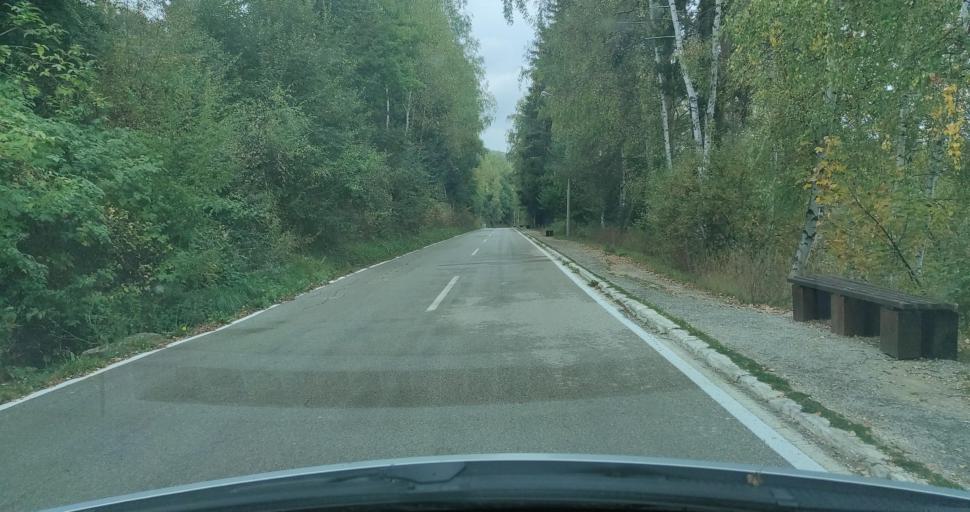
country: RS
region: Central Serbia
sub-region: Jablanicki Okrug
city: Crna Trava
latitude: 42.7442
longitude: 22.3274
